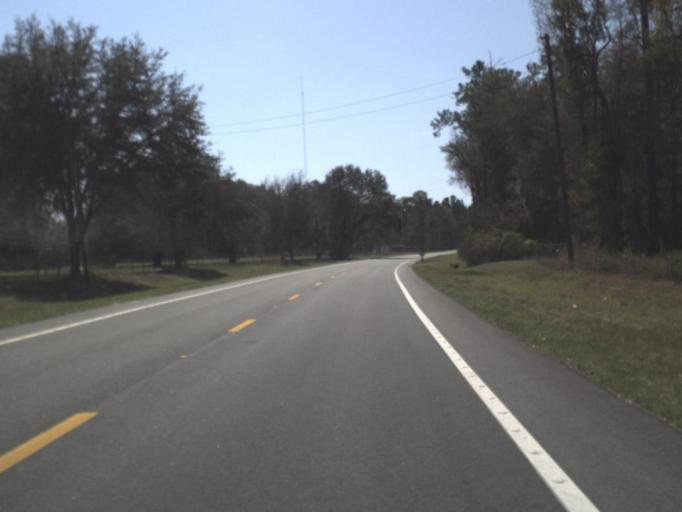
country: US
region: Florida
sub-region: Jefferson County
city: Monticello
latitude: 30.4708
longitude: -84.0205
